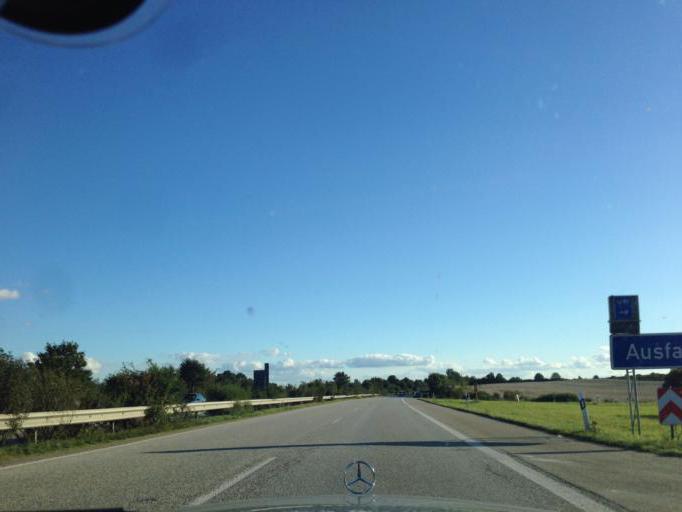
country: DE
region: Schleswig-Holstein
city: Hogersdorf
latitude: 53.9320
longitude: 10.2772
